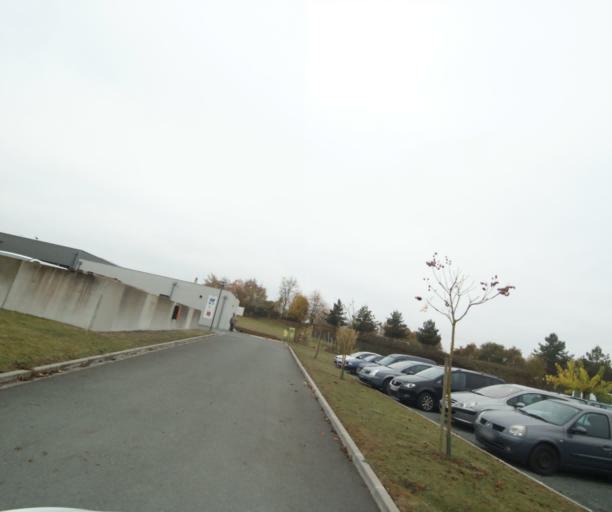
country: FR
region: Poitou-Charentes
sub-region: Departement de la Charente-Maritime
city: Saintes
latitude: 45.7519
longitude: -0.6703
